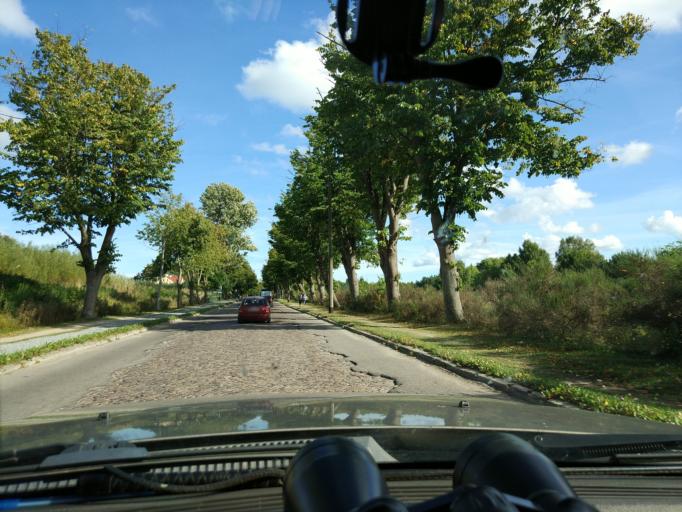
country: PL
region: Pomeranian Voivodeship
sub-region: Powiat pucki
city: Jastrzebia Gora
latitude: 54.8288
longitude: 18.3333
